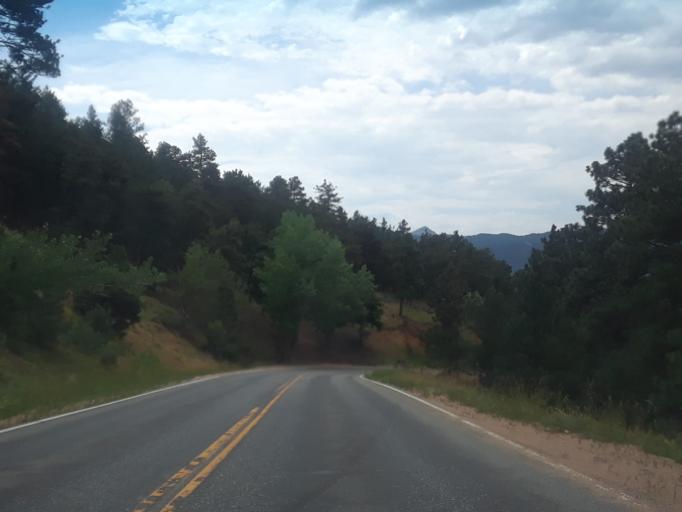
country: US
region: Colorado
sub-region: Boulder County
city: Boulder
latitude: 40.0394
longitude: -105.3281
